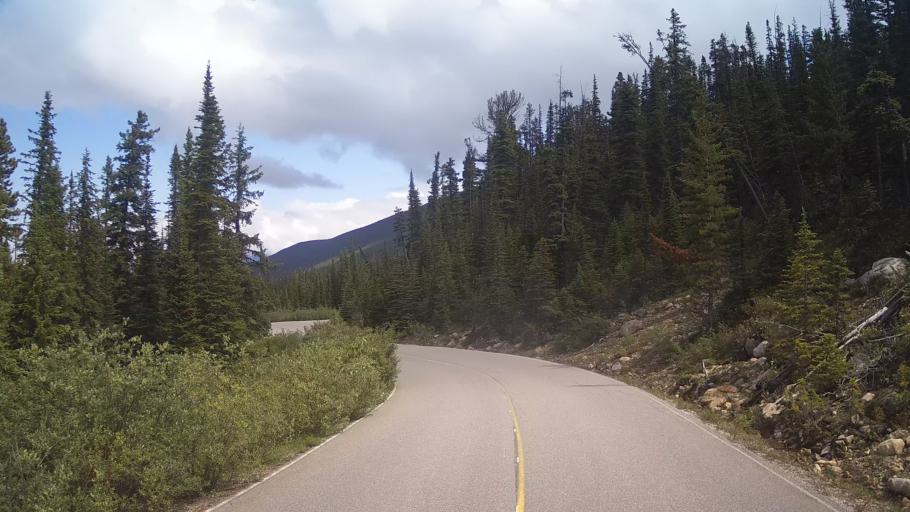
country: CA
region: Alberta
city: Jasper Park Lodge
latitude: 52.7072
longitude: -118.0578
